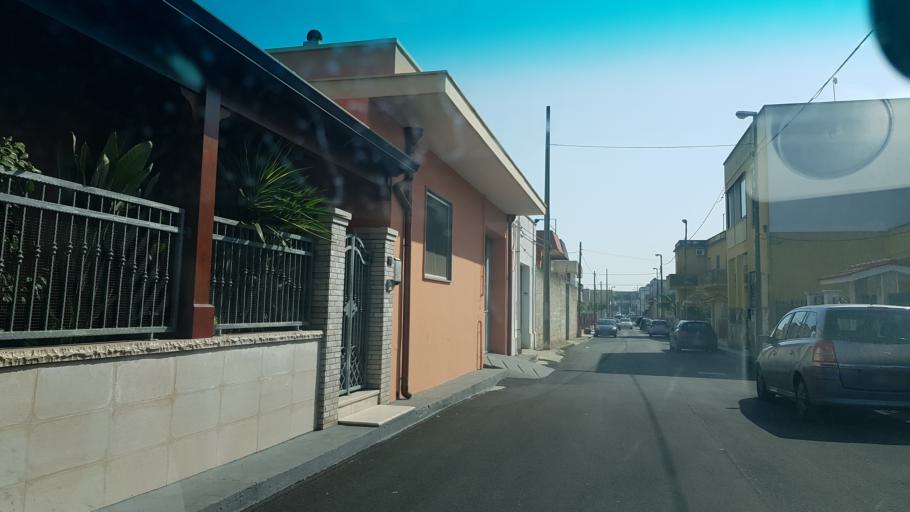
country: IT
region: Apulia
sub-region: Provincia di Brindisi
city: Torchiarolo
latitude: 40.4838
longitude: 18.0503
